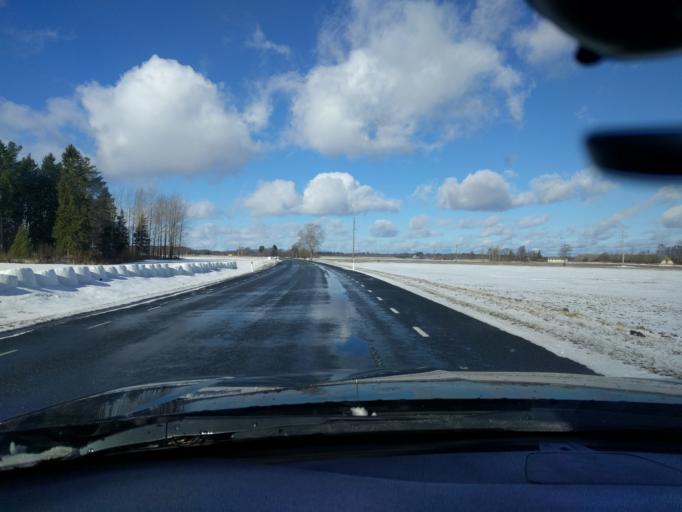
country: EE
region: Harju
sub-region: Anija vald
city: Kehra
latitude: 59.2474
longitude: 25.3498
